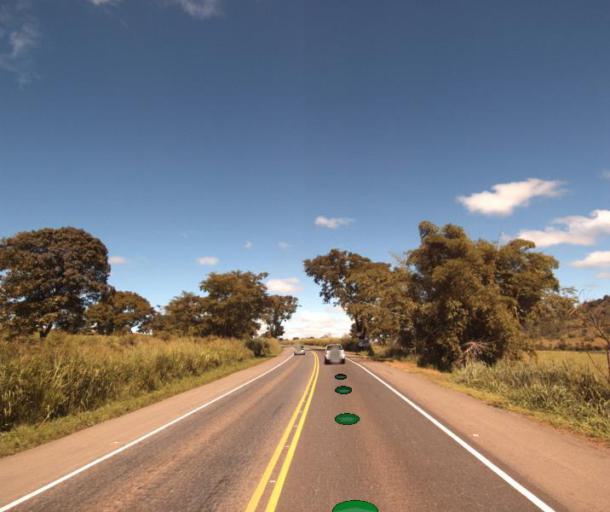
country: BR
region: Goias
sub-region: Rialma
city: Rialma
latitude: -15.2833
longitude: -49.5612
